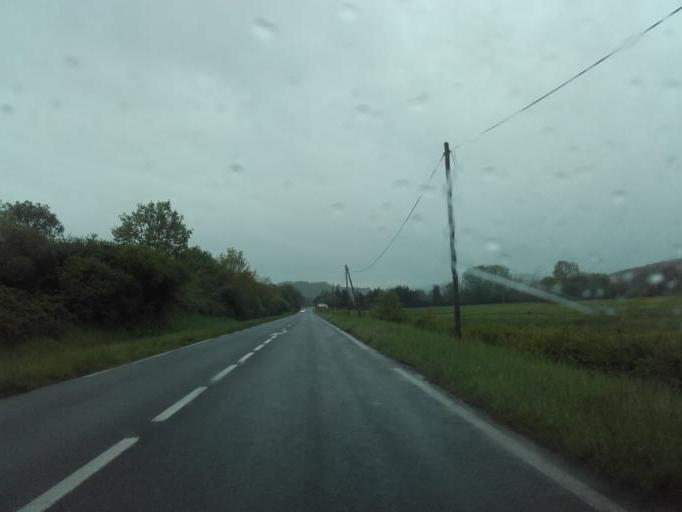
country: FR
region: Bourgogne
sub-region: Departement de Saone-et-Loire
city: Cluny
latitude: 46.4180
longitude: 4.6620
